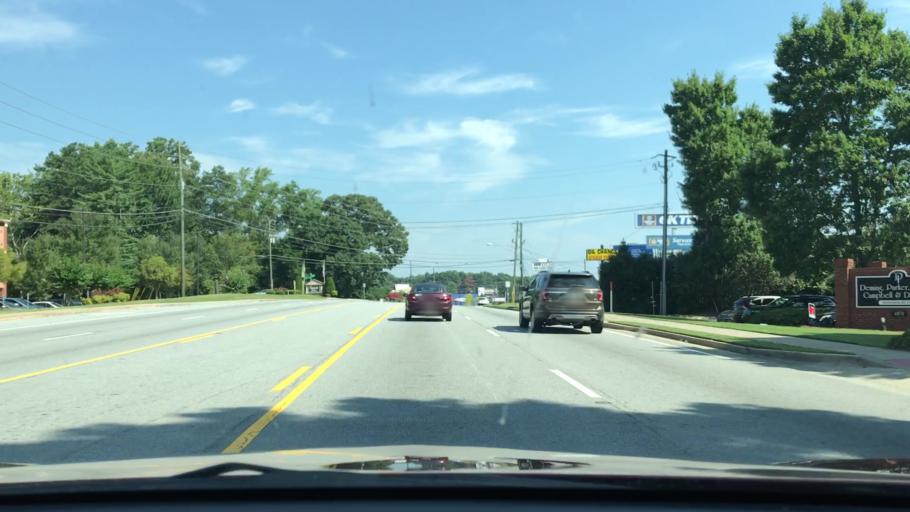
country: US
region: Georgia
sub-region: DeKalb County
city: Tucker
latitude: 33.8918
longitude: -84.1957
